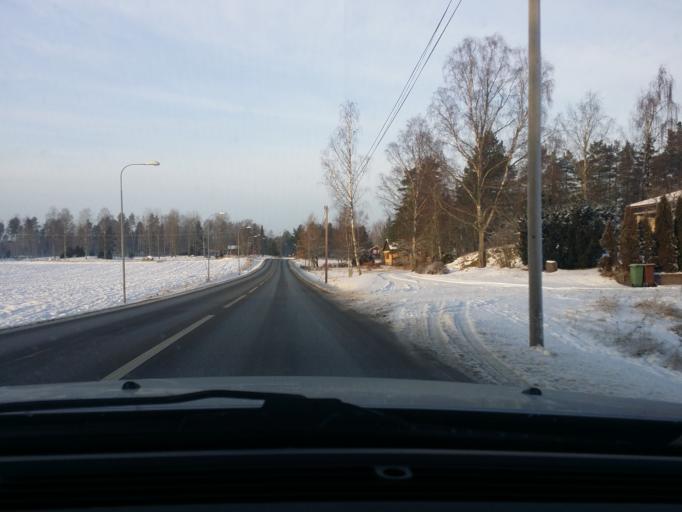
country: SE
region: OErebro
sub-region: Lindesbergs Kommun
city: Frovi
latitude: 59.5218
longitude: 15.3126
